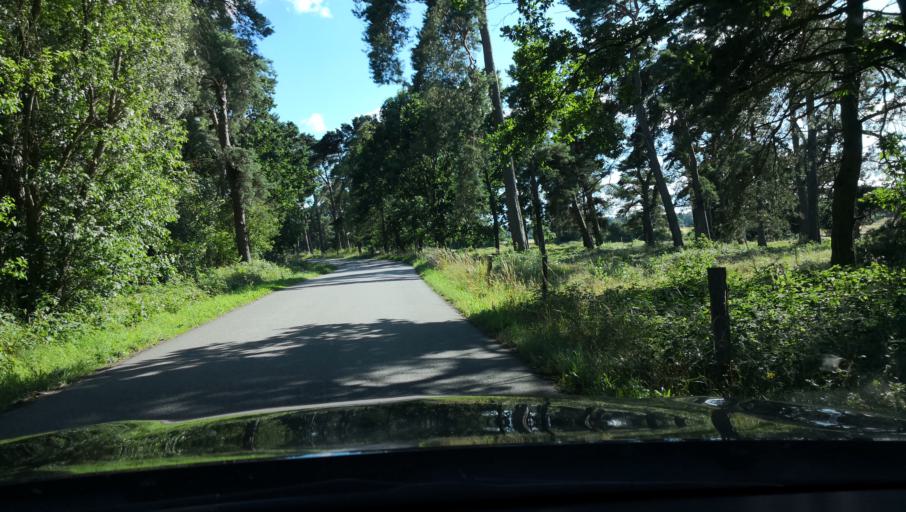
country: SE
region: Skane
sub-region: Simrishamns Kommun
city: Kivik
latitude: 55.7882
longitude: 14.1965
